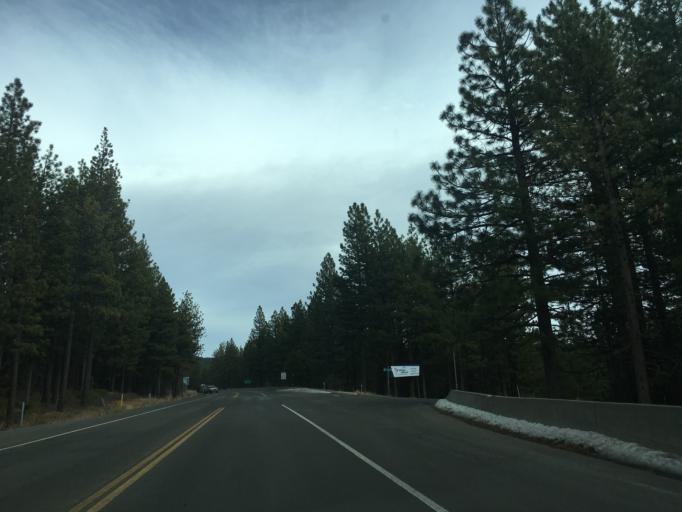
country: US
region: Nevada
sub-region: Washoe County
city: Incline Village
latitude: 39.2554
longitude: -119.9655
